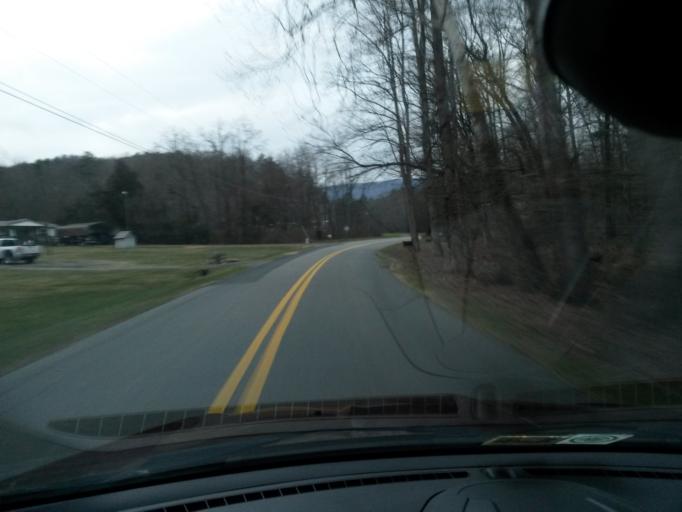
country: US
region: Virginia
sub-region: Alleghany County
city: Clifton Forge
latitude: 37.8501
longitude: -79.8064
